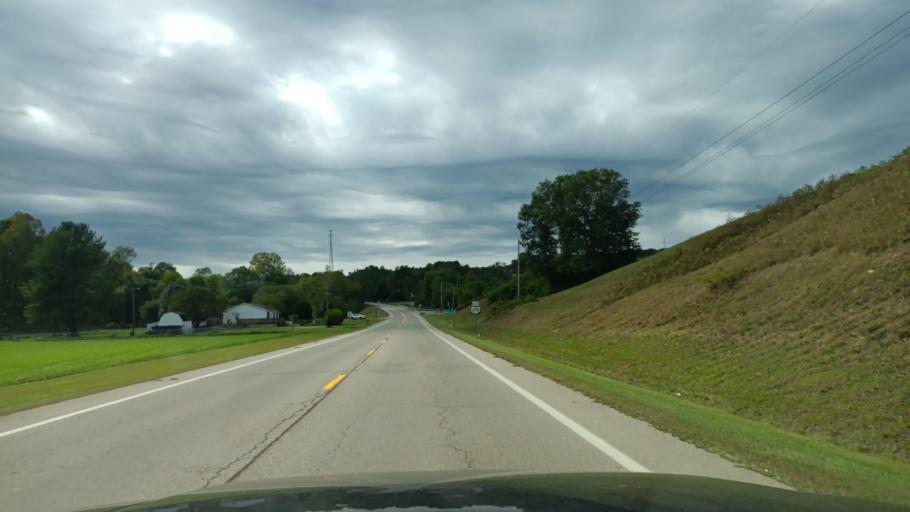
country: US
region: Ohio
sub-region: Vinton County
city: McArthur
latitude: 39.2384
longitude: -82.3830
